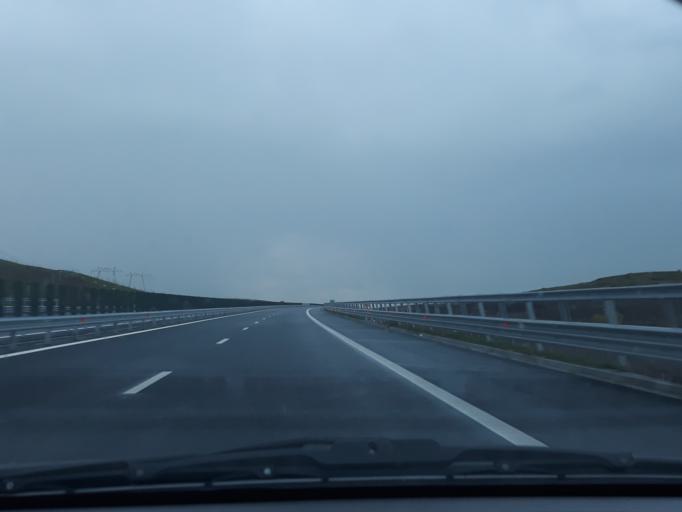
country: RO
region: Mures
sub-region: Comuna Sanpaul
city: Sanpaul
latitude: 46.4391
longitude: 24.3375
